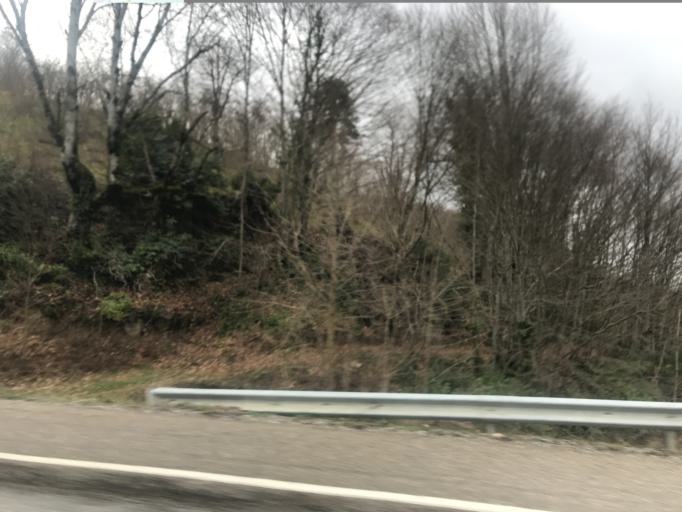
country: TR
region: Bartin
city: Amasra
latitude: 41.7068
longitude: 32.3890
